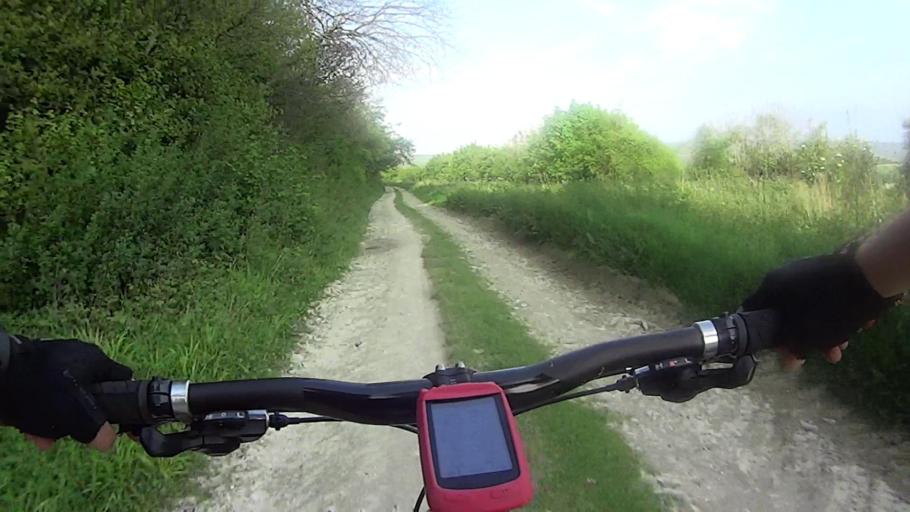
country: GB
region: England
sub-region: West Sussex
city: Arundel
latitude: 50.8978
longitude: -0.5704
